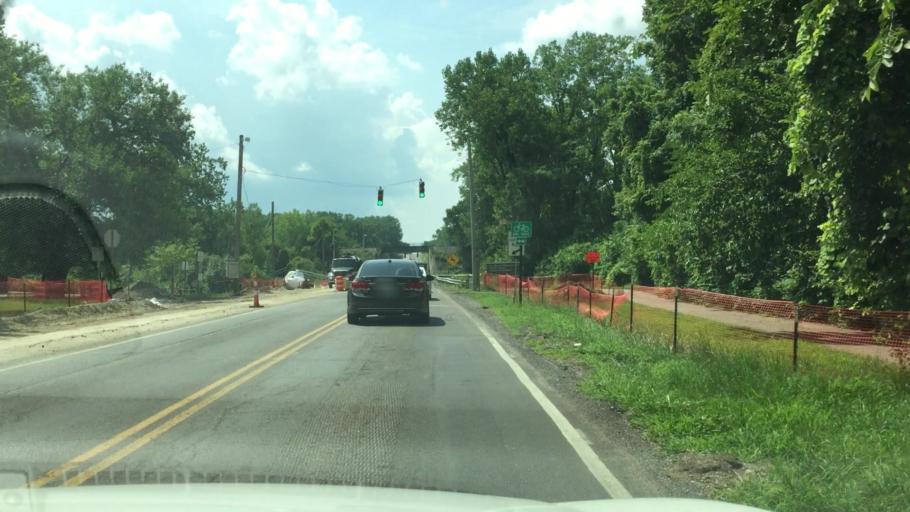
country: US
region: Ohio
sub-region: Clark County
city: Northridge
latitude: 39.9502
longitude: -83.7549
